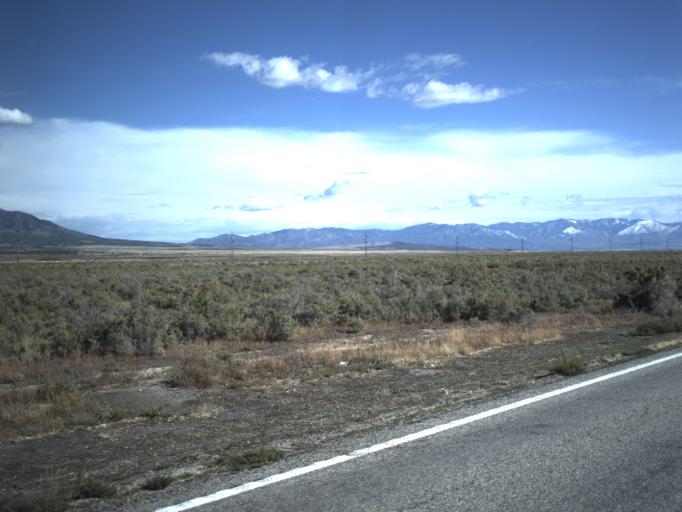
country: US
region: Utah
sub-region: Millard County
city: Delta
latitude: 39.2836
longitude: -112.4619
